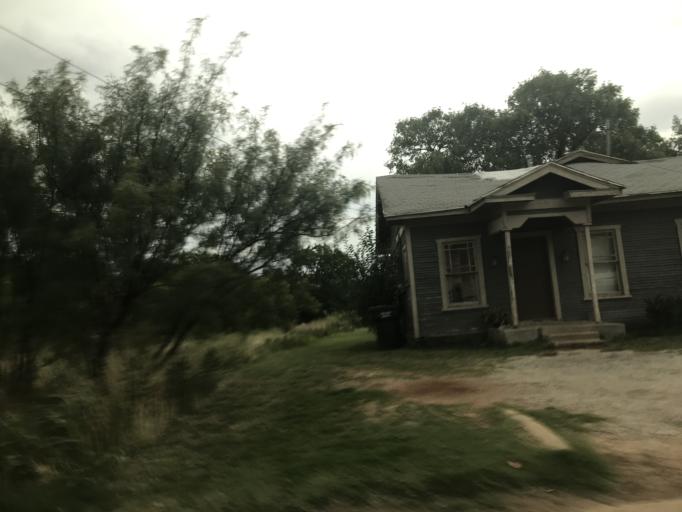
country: US
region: Texas
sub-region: Taylor County
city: Abilene
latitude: 32.4465
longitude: -99.7555
